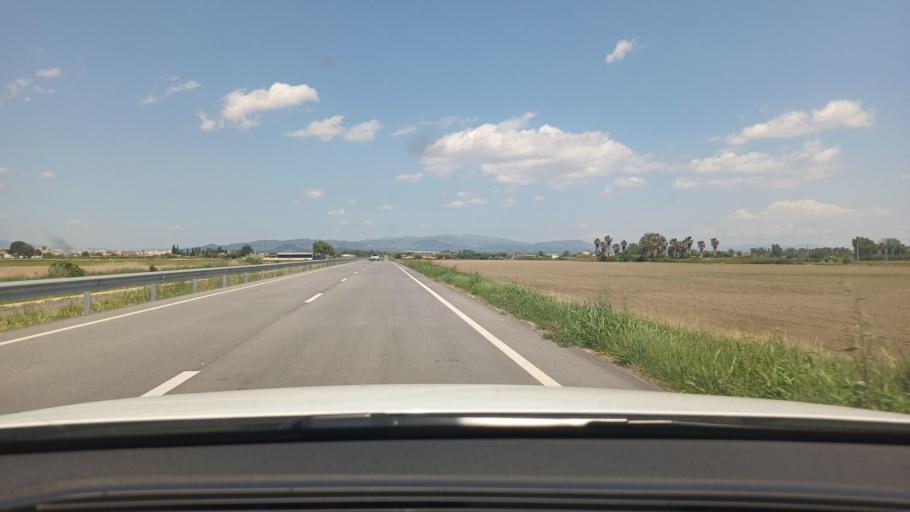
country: ES
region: Catalonia
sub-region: Provincia de Tarragona
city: Amposta
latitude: 40.6865
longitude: 0.5905
